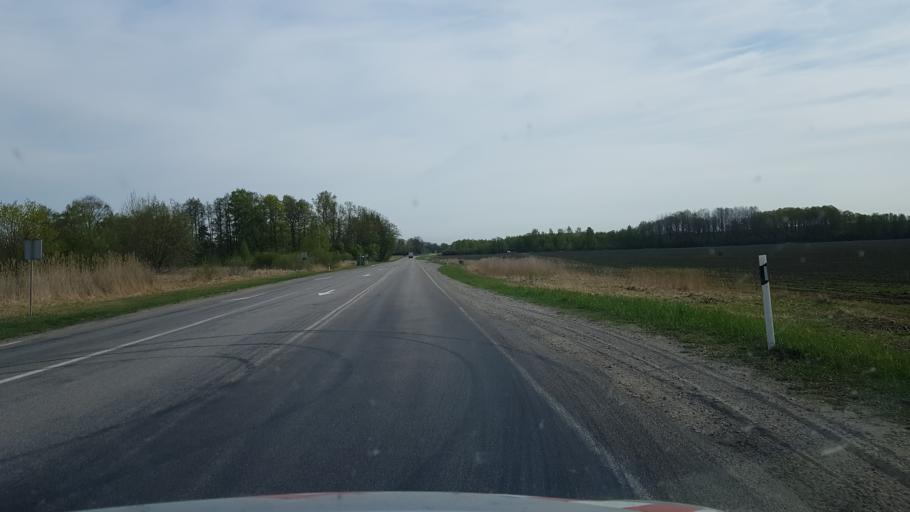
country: EE
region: Paernumaa
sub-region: Audru vald
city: Audru
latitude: 58.3926
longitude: 24.2794
